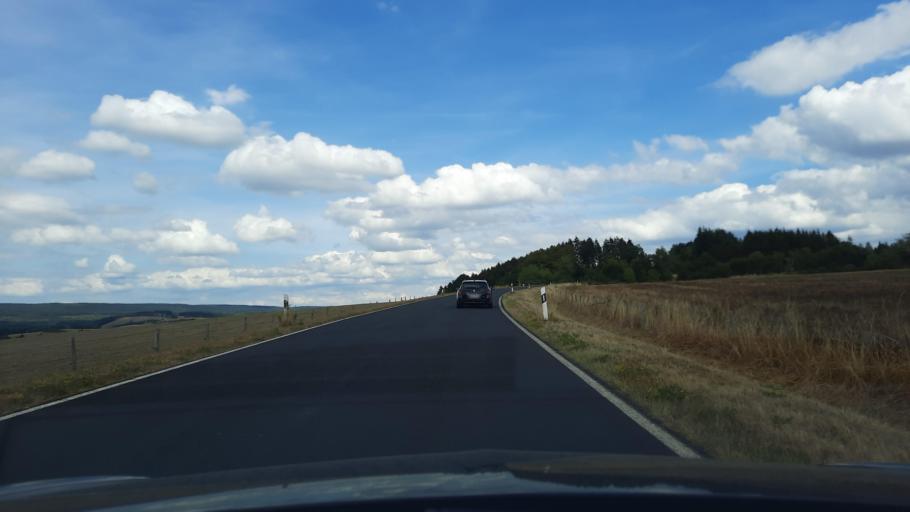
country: DE
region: Rheinland-Pfalz
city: Watzerath
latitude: 50.2062
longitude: 6.3689
